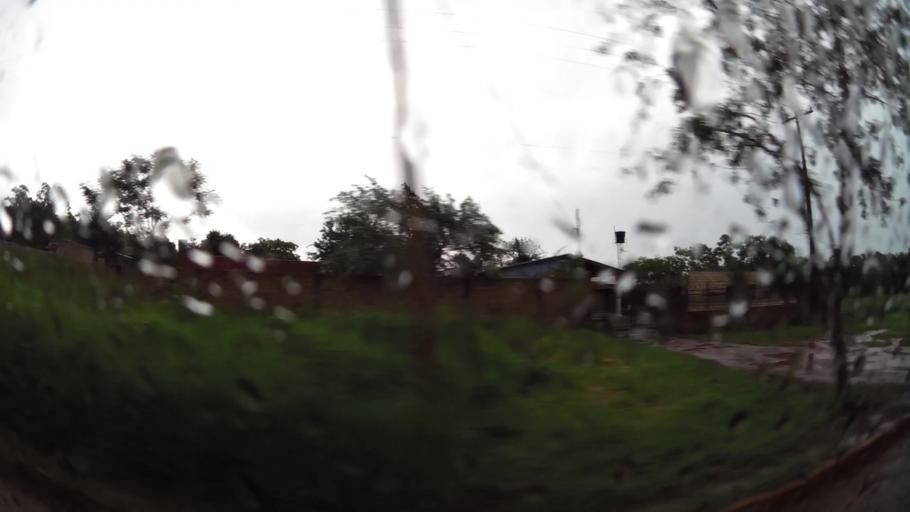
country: PY
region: Alto Parana
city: Presidente Franco
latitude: -25.5313
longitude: -54.6801
